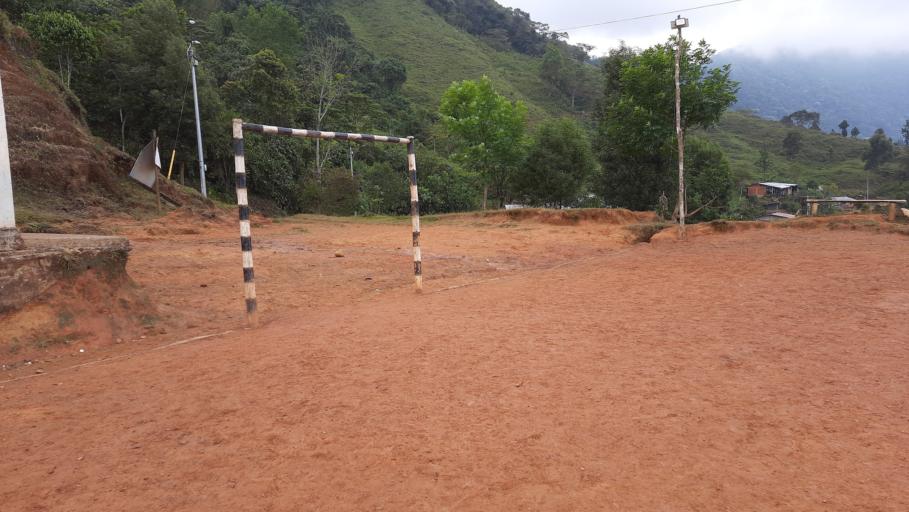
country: CO
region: Cauca
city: Buenos Aires
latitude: 3.1779
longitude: -76.7238
